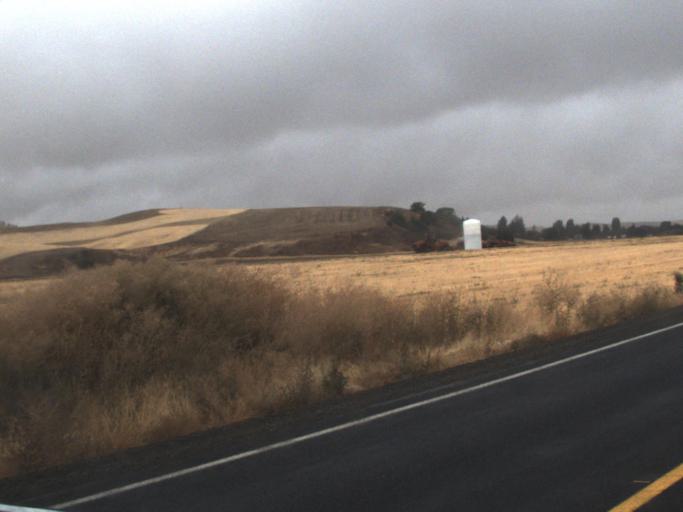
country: US
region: Washington
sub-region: Whitman County
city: Colfax
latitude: 47.0880
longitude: -117.5605
